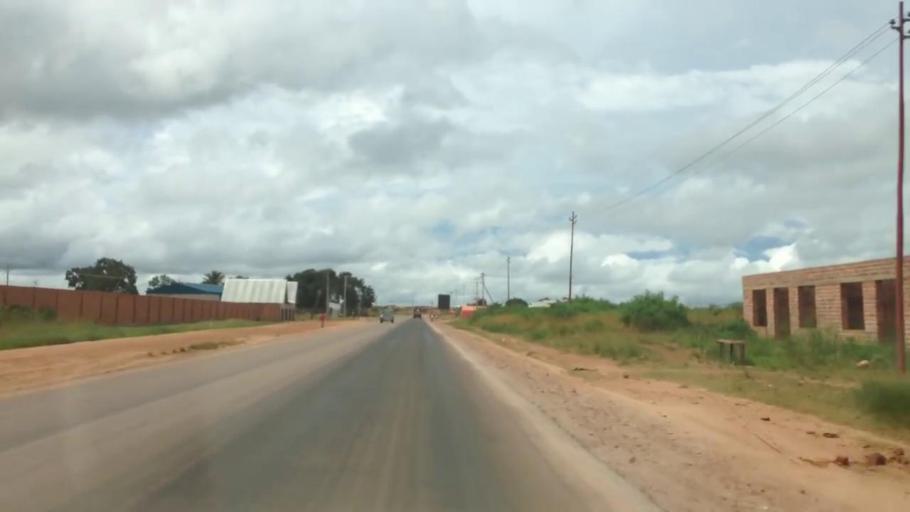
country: CD
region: Katanga
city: Kolwezi
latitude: -10.7383
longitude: 25.5117
